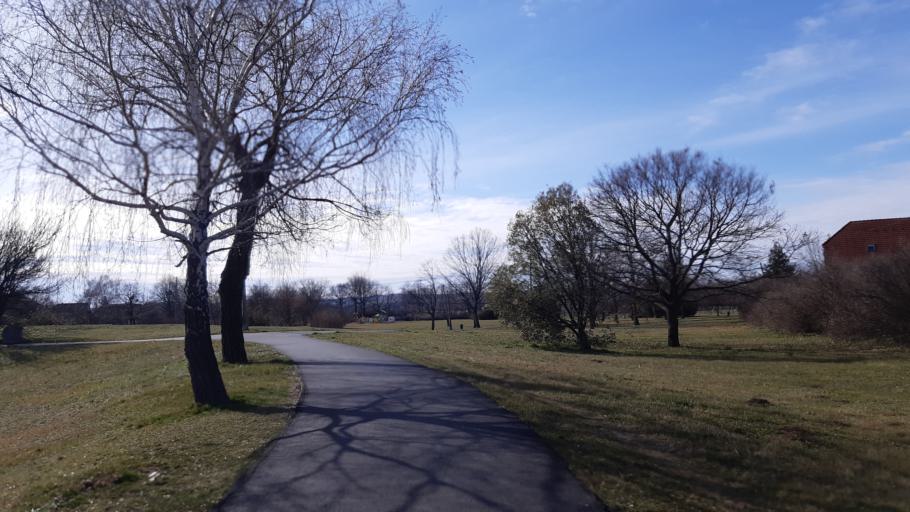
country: HU
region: Baranya
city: Pellerd
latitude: 46.0623
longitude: 18.1837
